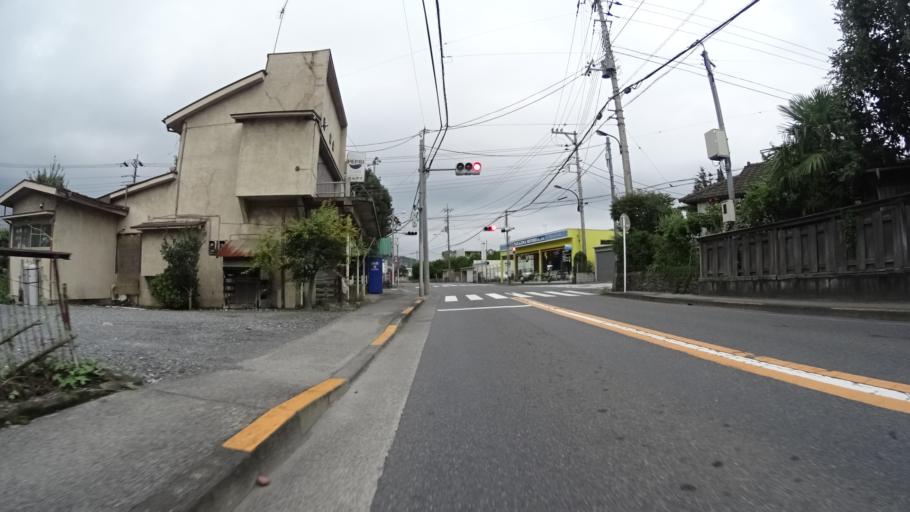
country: JP
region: Tokyo
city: Fussa
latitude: 35.7609
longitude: 139.3048
